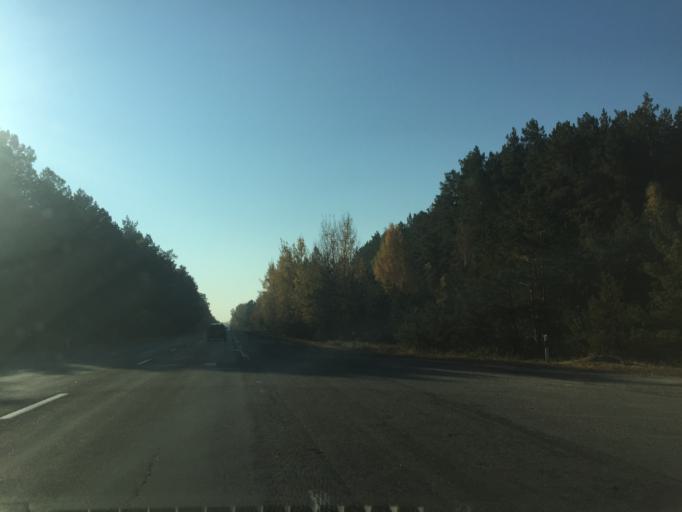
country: BY
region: Gomel
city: Kastsyukowka
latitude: 52.4341
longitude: 30.8267
